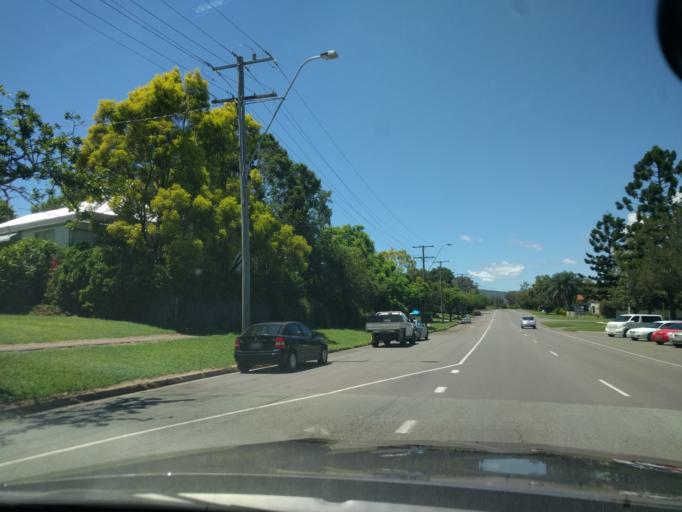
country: AU
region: Queensland
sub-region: Logan
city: Cedar Vale
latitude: -27.9907
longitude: 152.9962
